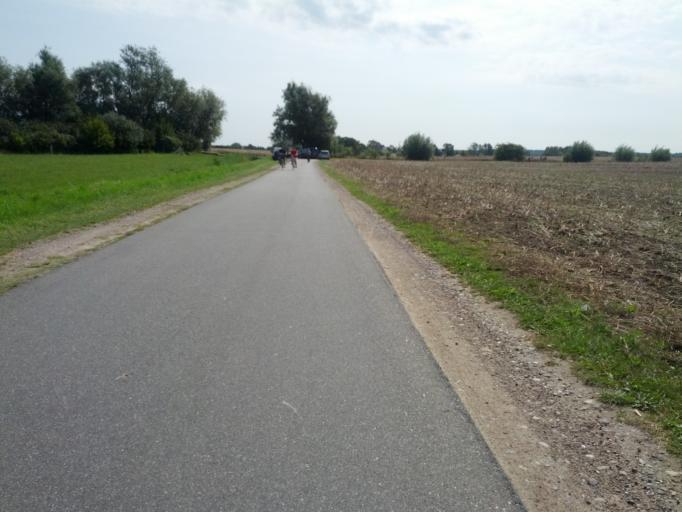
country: DE
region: Mecklenburg-Vorpommern
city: Bastorf
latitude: 54.1480
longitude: 11.6930
